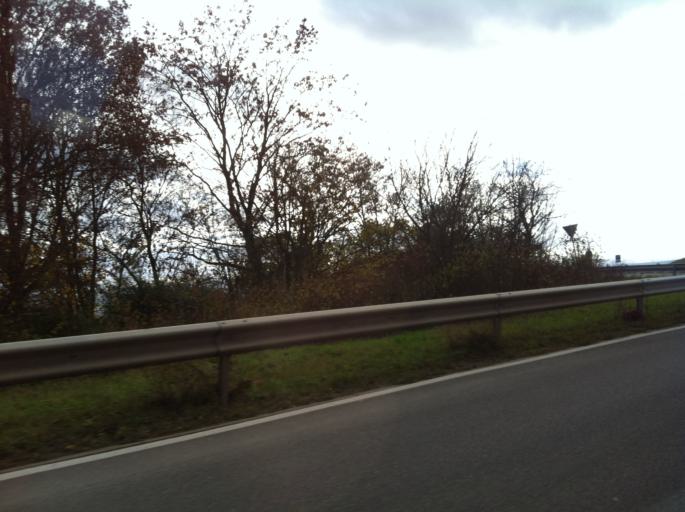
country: DE
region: Rheinland-Pfalz
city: Essenheim
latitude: 49.9374
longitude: 8.1657
